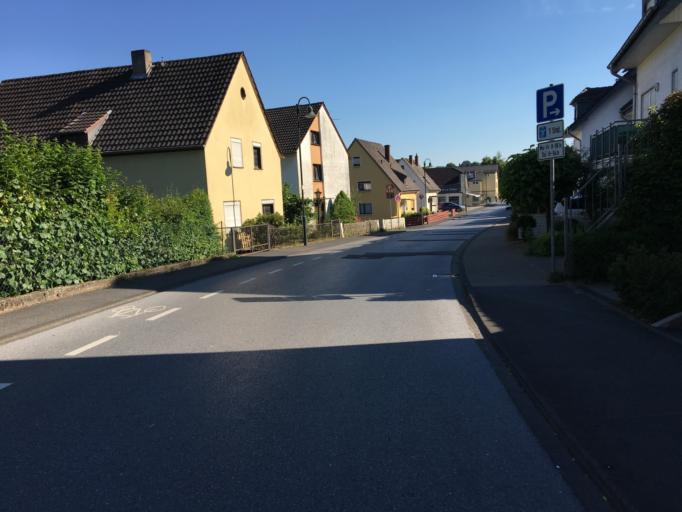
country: DE
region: North Rhine-Westphalia
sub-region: Regierungsbezirk Koln
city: Rosrath
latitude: 50.8950
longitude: 7.1820
